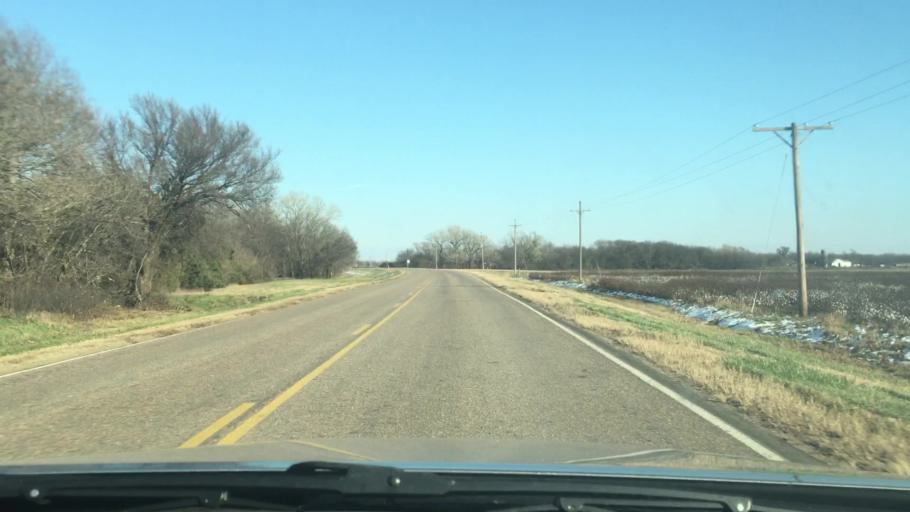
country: US
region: Kansas
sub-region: Rice County
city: Lyons
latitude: 38.2893
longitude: -98.1489
